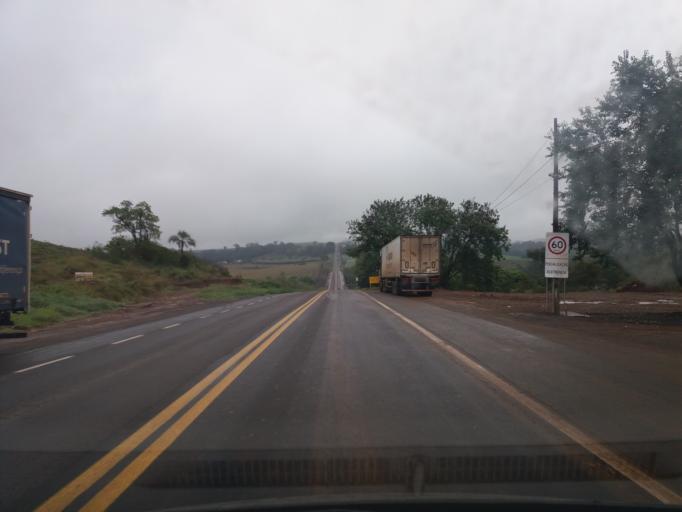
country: BR
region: Parana
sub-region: Realeza
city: Realeza
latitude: -25.5667
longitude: -53.5751
